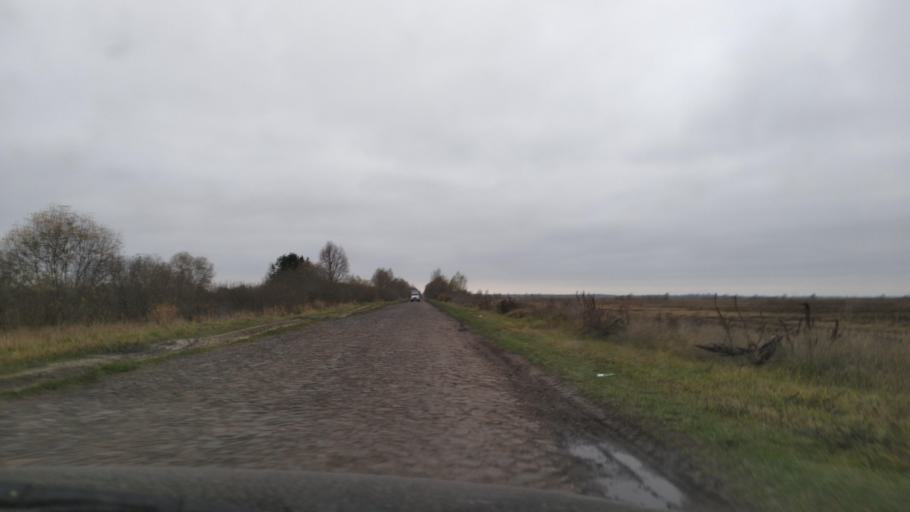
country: BY
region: Brest
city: Davyd-Haradok
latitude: 52.0039
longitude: 27.2055
